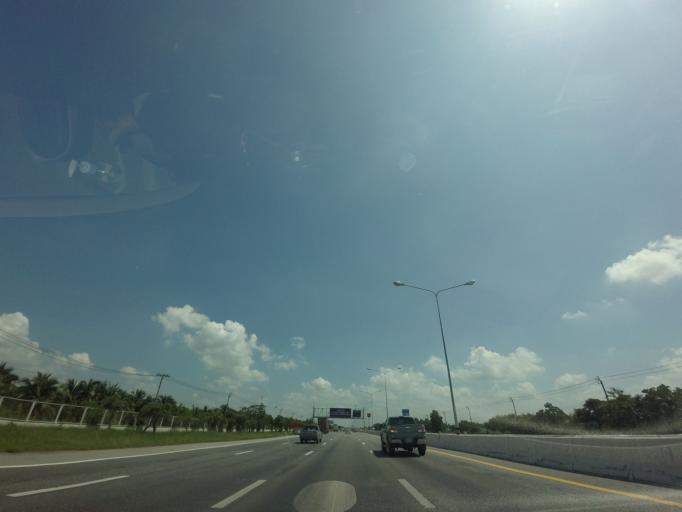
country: TH
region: Samut Prakan
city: Ban Khlong Bang Sao Thong
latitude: 13.6231
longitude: 100.9170
